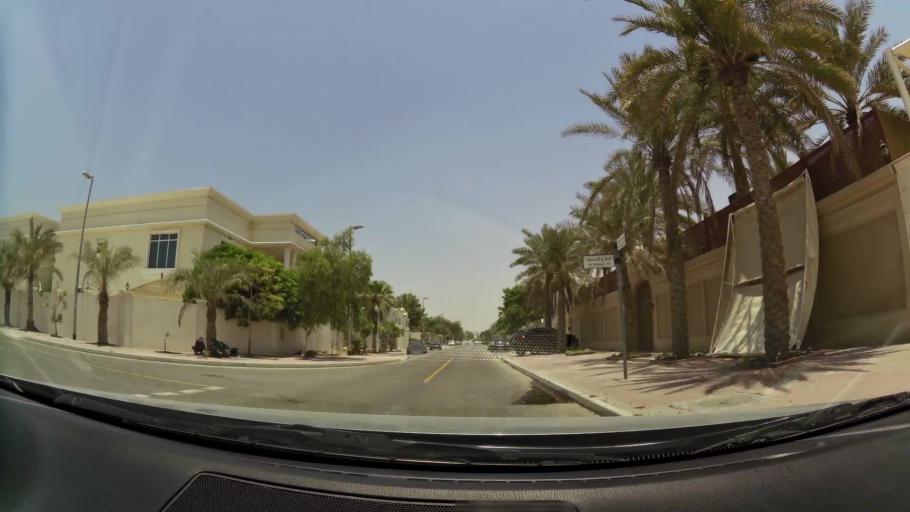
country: AE
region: Dubai
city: Dubai
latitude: 25.1768
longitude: 55.2235
